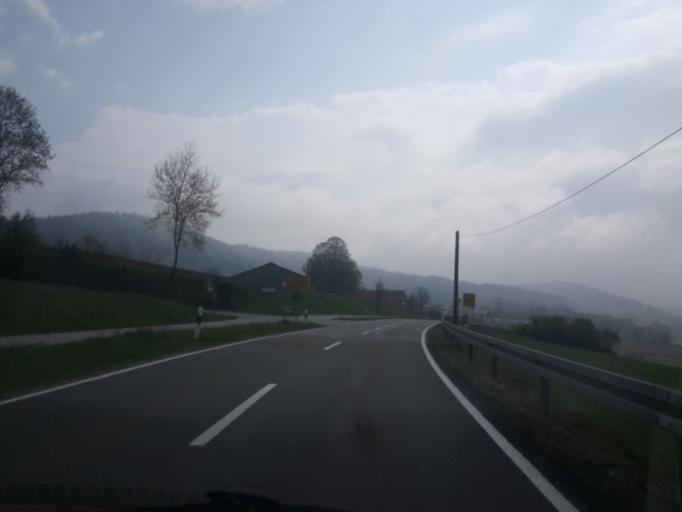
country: DE
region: Bavaria
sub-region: Lower Bavaria
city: Geiersthal
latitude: 49.0568
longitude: 12.9607
